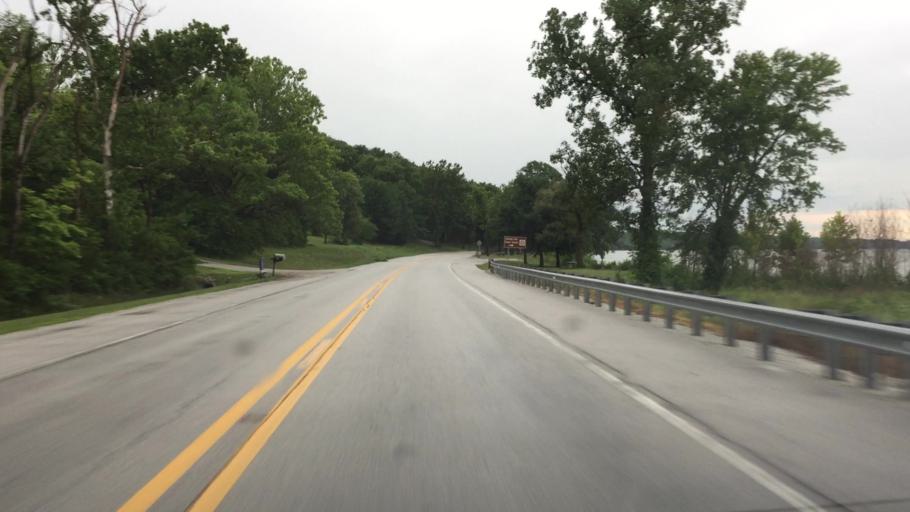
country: US
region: Illinois
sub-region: Hancock County
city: Nauvoo
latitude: 40.5100
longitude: -91.3579
